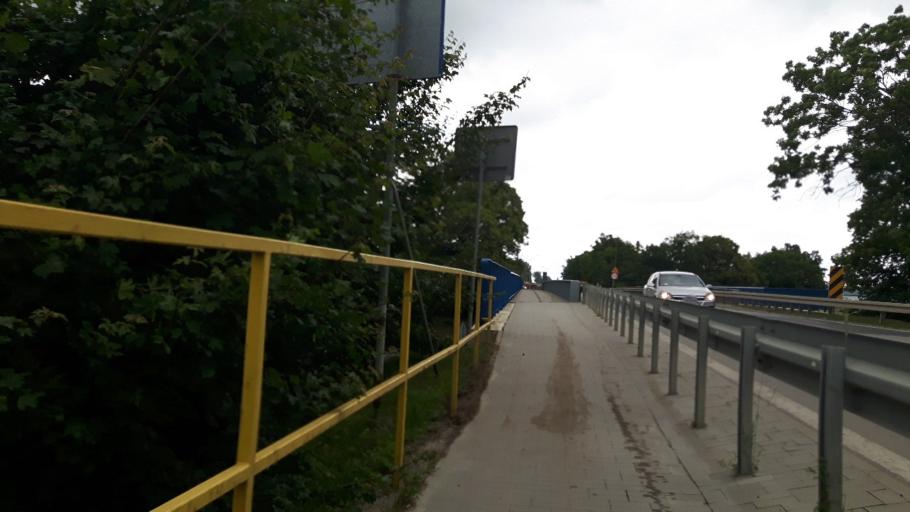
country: PL
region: West Pomeranian Voivodeship
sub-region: Powiat policki
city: Kolbaskowo
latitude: 53.3402
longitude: 14.4430
